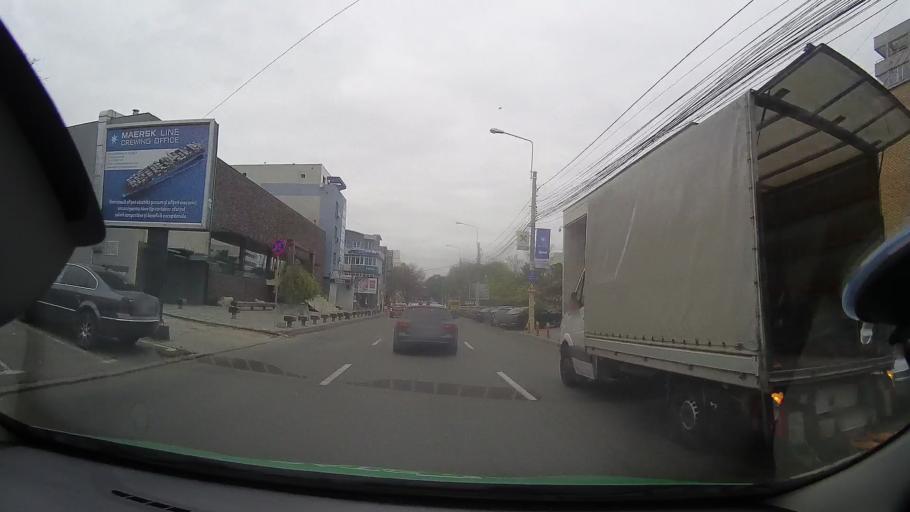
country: RO
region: Constanta
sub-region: Municipiul Constanta
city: Constanta
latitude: 44.1820
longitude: 28.6506
